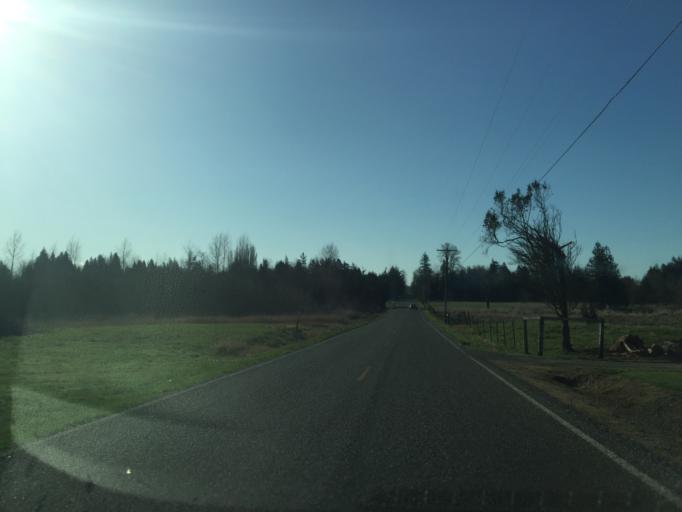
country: US
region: Washington
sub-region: Whatcom County
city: Lynden
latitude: 48.8652
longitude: -122.4970
